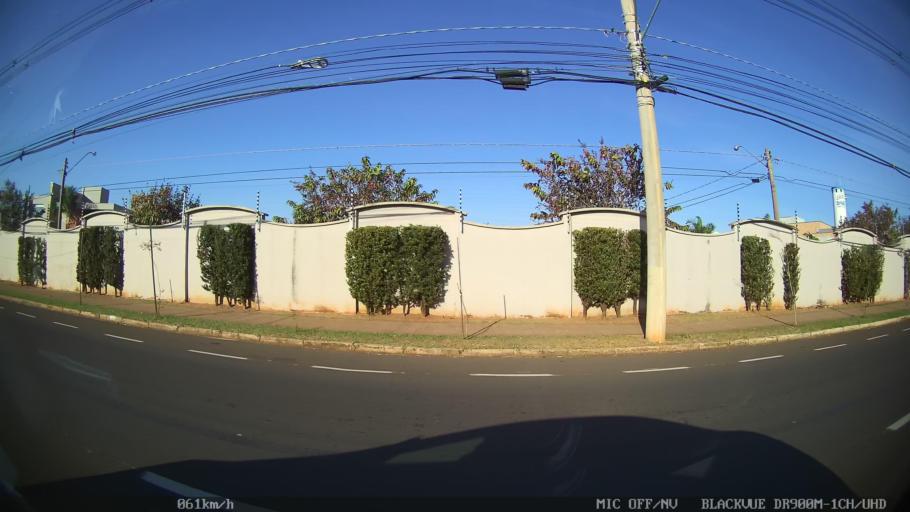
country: BR
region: Sao Paulo
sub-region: Sao Jose Do Rio Preto
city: Sao Jose do Rio Preto
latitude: -20.8633
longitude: -49.4122
